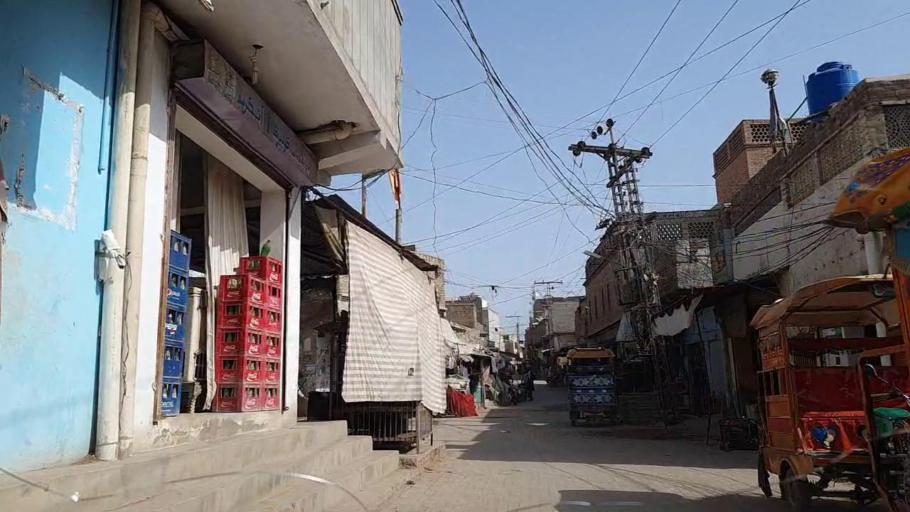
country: PK
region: Sindh
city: Kandiaro
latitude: 27.0621
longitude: 68.2074
